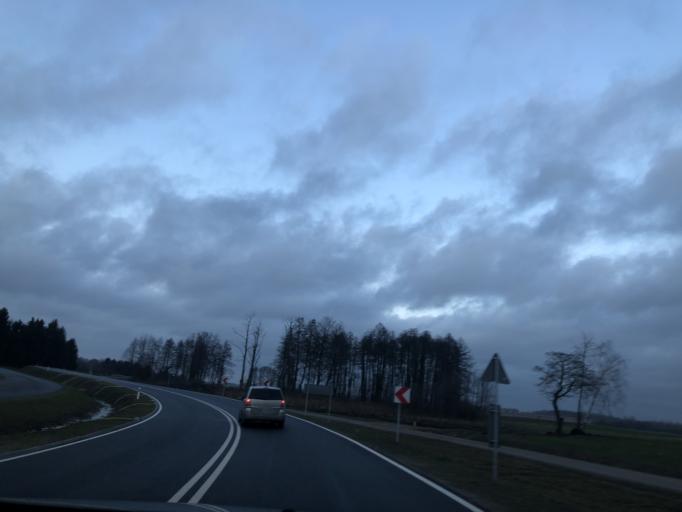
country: PL
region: Podlasie
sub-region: Lomza
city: Lomza
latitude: 53.1260
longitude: 22.0486
